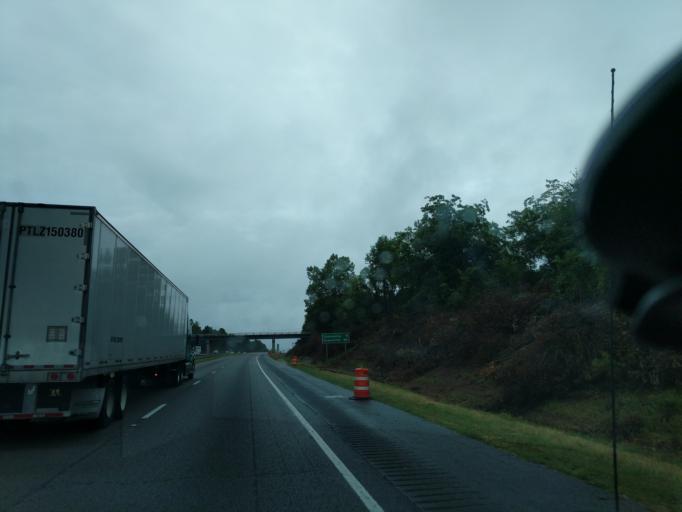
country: US
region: Georgia
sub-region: Banks County
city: Maysville
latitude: 34.1933
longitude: -83.5807
